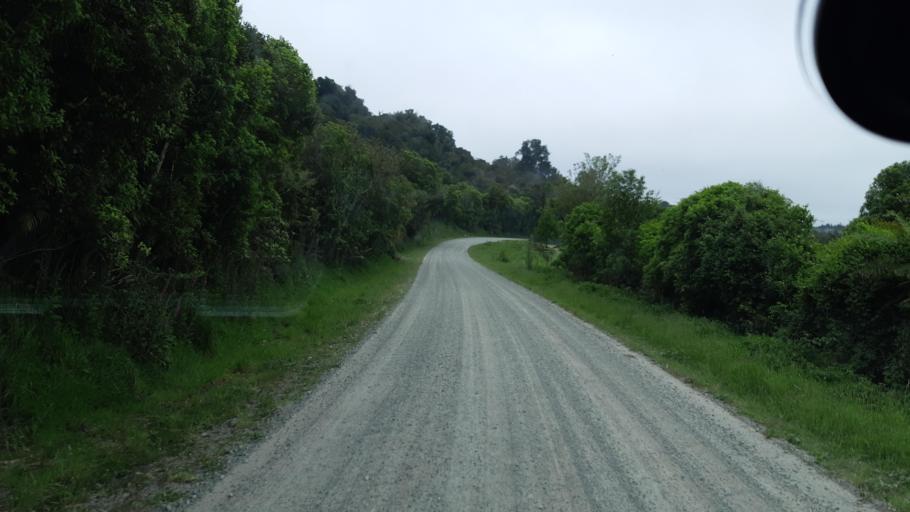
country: NZ
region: West Coast
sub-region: Grey District
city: Greymouth
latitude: -42.6385
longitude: 171.3911
